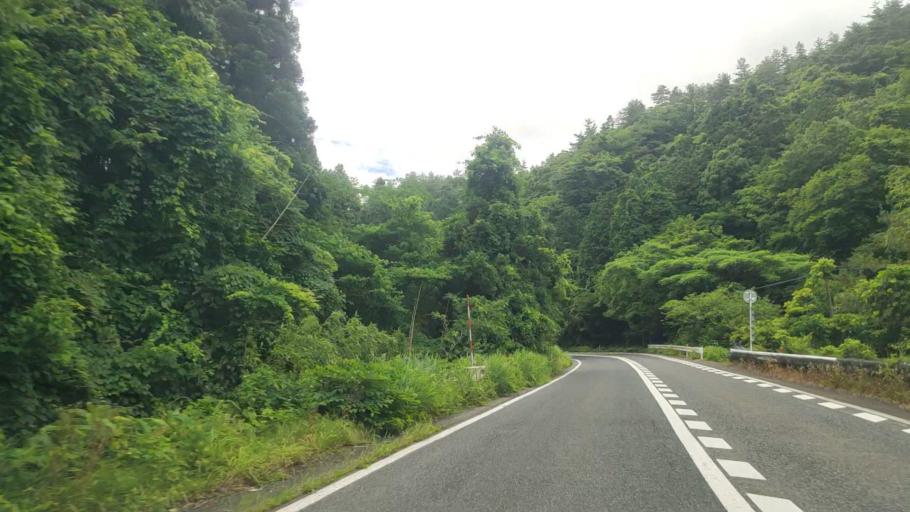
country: JP
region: Tottori
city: Yonago
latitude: 35.2763
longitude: 133.4320
